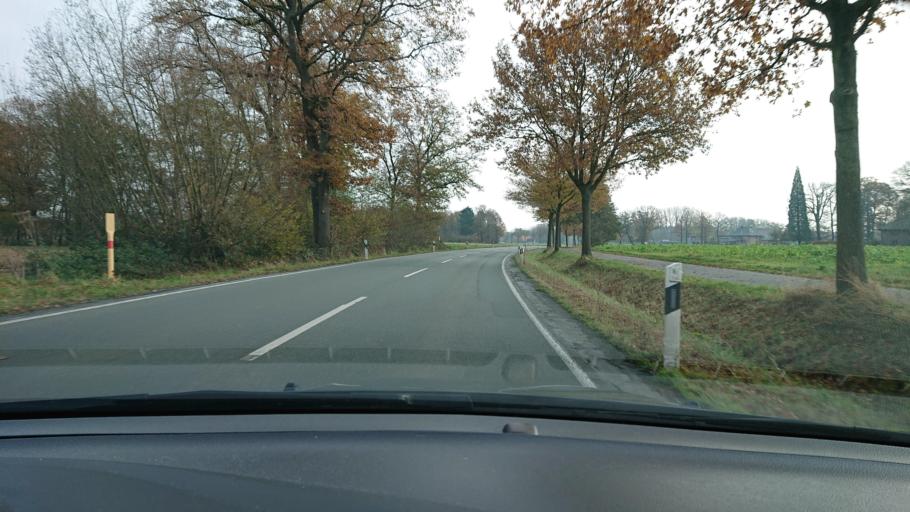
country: DE
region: North Rhine-Westphalia
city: Rietberg
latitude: 51.8143
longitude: 8.4621
